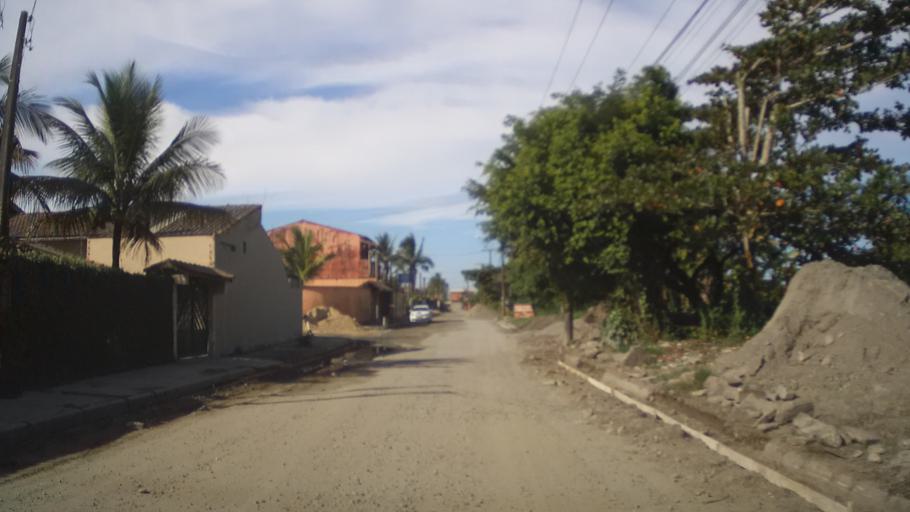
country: BR
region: Sao Paulo
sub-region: Itanhaem
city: Itanhaem
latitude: -24.2097
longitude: -46.8422
